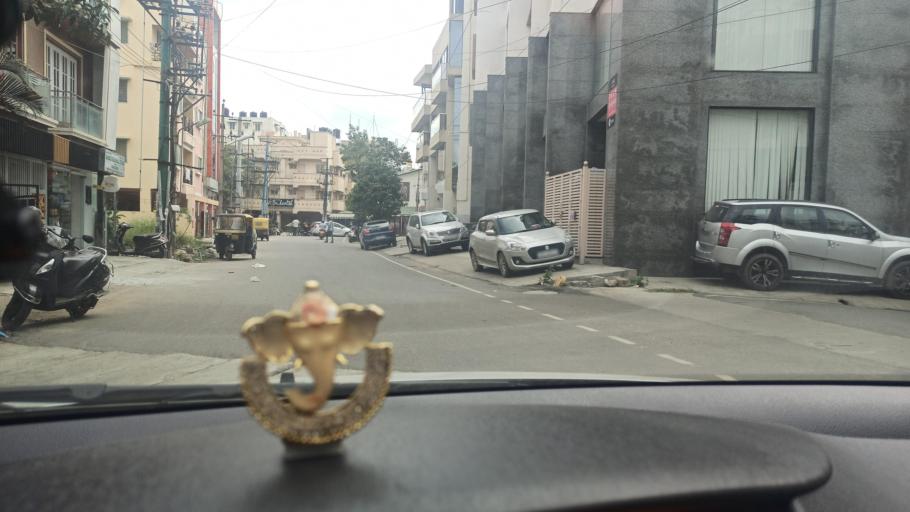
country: IN
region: Karnataka
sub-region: Bangalore Urban
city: Bangalore
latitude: 12.9117
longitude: 77.6317
